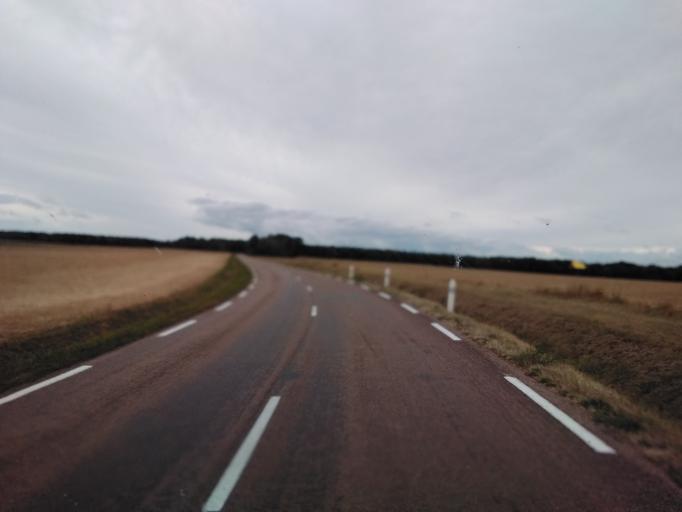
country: FR
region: Champagne-Ardenne
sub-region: Departement de l'Aube
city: Vendeuvre-sur-Barse
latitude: 48.2245
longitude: 4.4524
